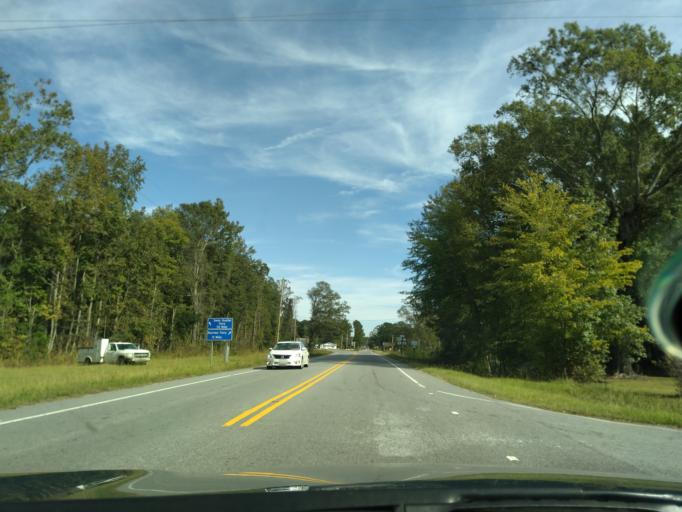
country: US
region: North Carolina
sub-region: Beaufort County
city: River Road
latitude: 35.5120
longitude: -76.9059
